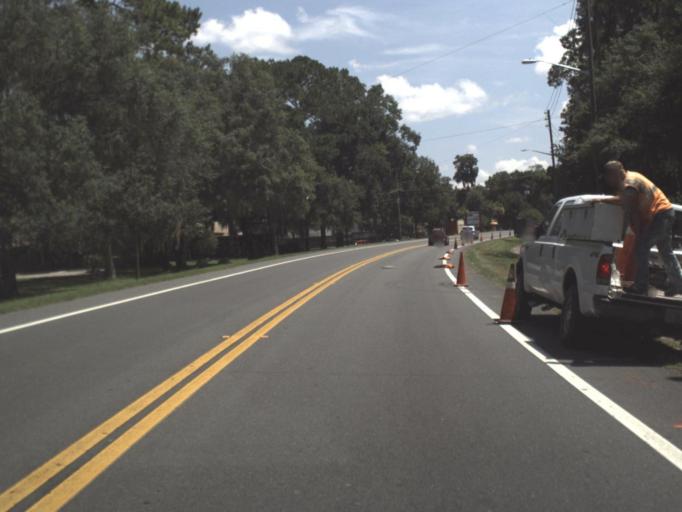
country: US
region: Florida
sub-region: Alachua County
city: Gainesville
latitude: 29.6982
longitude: -82.3718
